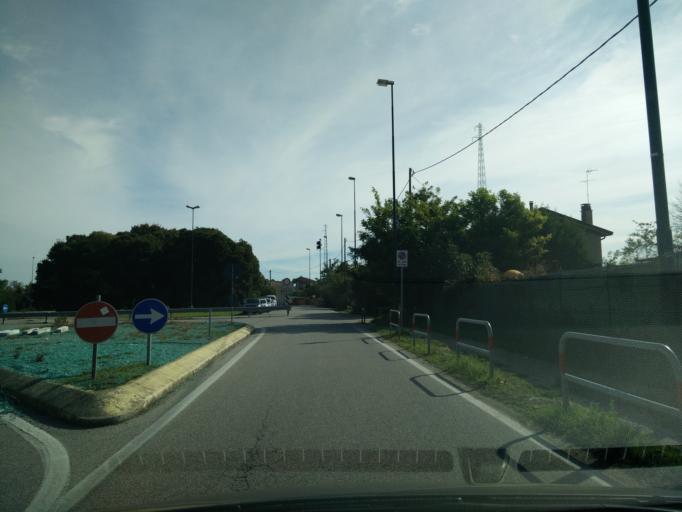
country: IT
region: Veneto
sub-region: Provincia di Venezia
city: Mestre
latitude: 45.4192
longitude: 12.2564
